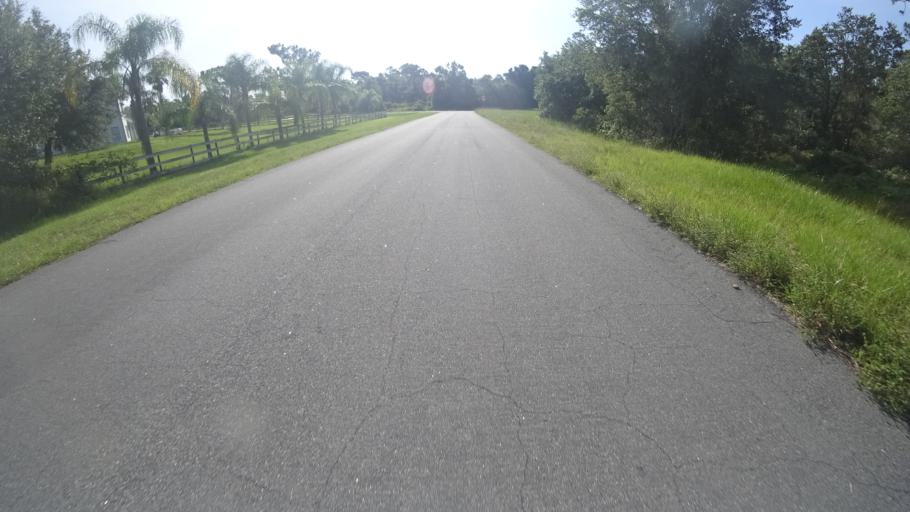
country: US
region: Florida
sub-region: Sarasota County
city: Lake Sarasota
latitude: 27.3518
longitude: -82.2474
